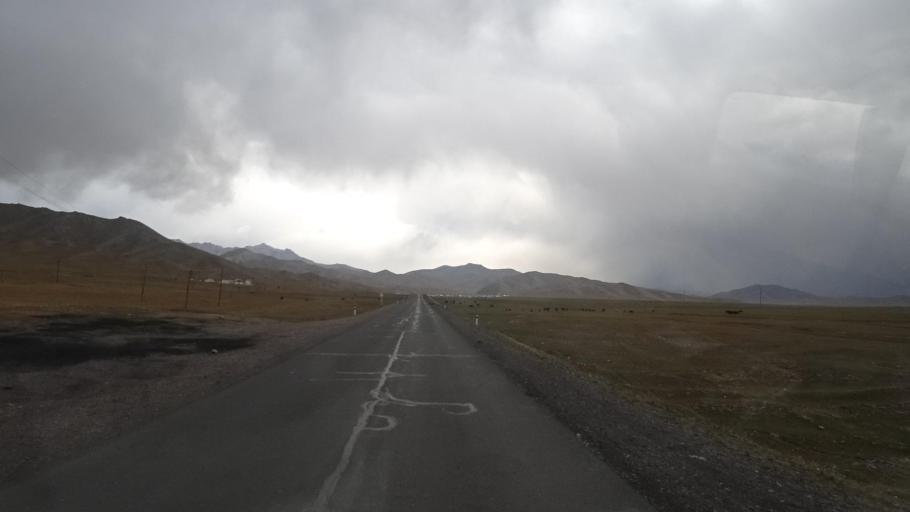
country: KG
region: Osh
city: Gul'cha
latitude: 39.7065
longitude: 73.2300
